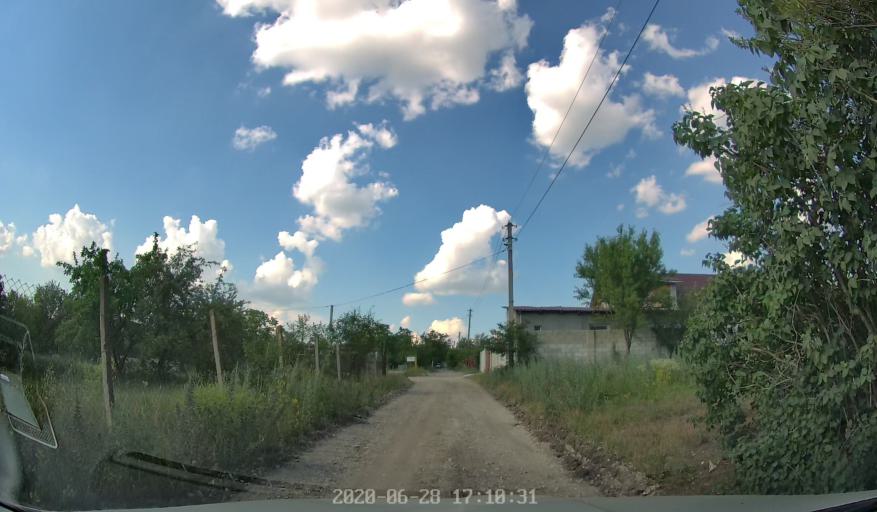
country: MD
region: Laloveni
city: Ialoveni
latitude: 46.9862
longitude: 28.7005
